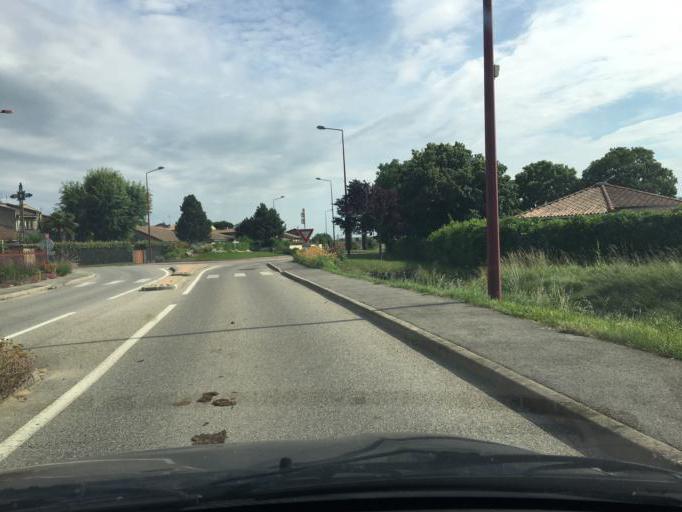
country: FR
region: Rhone-Alpes
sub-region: Departement de la Drome
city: Mercurol
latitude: 45.0761
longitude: 4.8896
